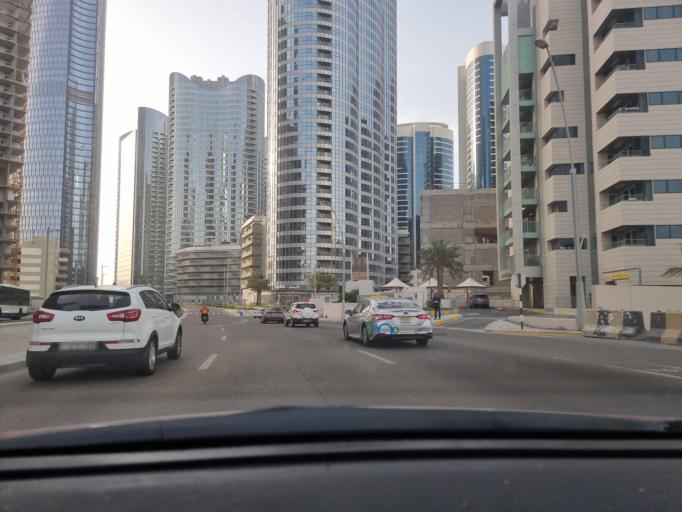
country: AE
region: Abu Dhabi
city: Abu Dhabi
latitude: 24.4969
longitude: 54.4057
